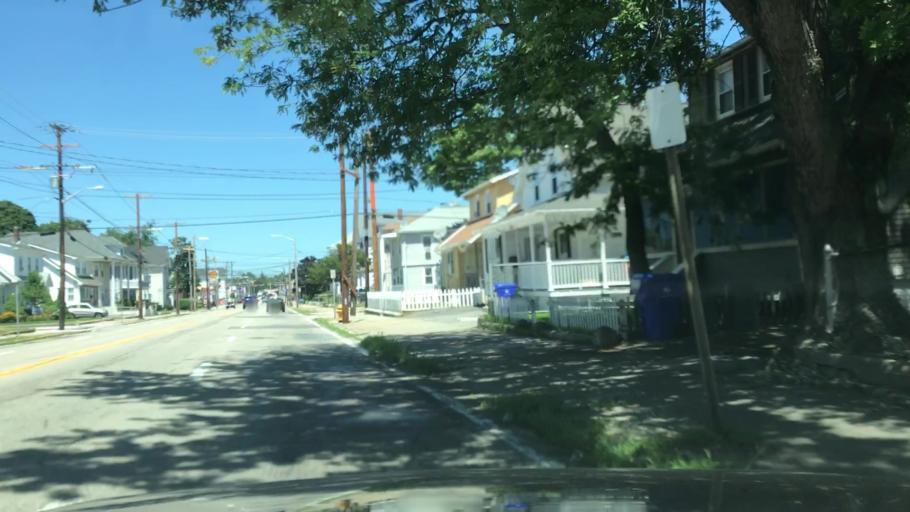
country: US
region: Massachusetts
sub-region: Bristol County
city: North Seekonk
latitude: 41.8897
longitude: -71.3541
